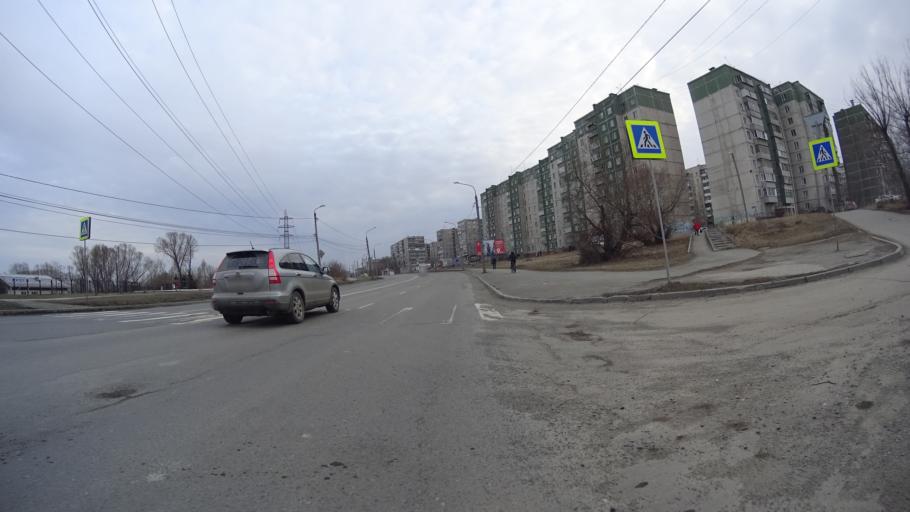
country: RU
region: Chelyabinsk
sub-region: Gorod Chelyabinsk
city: Chelyabinsk
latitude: 55.1866
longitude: 61.4845
